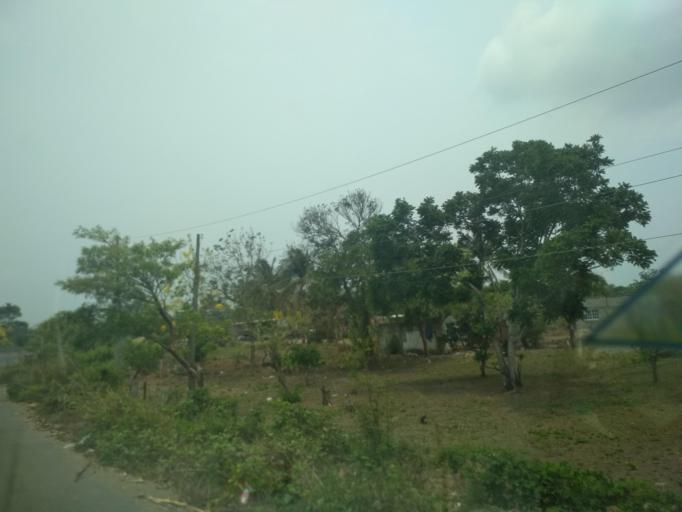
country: MX
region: Veracruz
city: Paso del Toro
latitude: 19.0344
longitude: -96.1503
